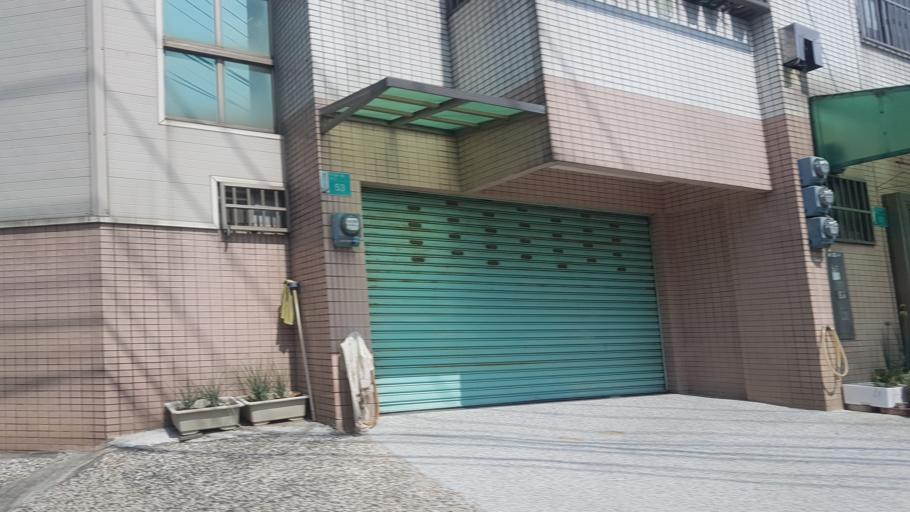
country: TW
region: Taiwan
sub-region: Tainan
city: Tainan
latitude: 22.9363
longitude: 120.2488
